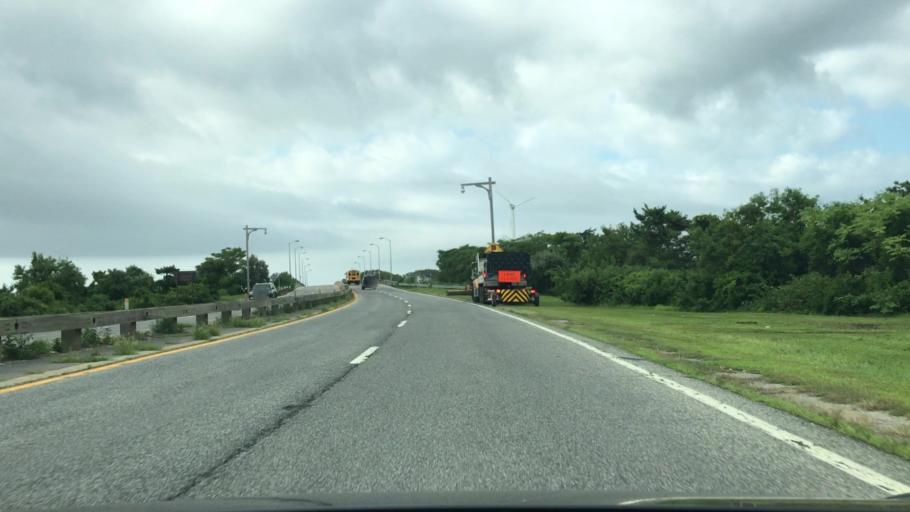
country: US
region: New York
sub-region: Nassau County
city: Point Lookout
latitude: 40.5966
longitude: -73.5872
